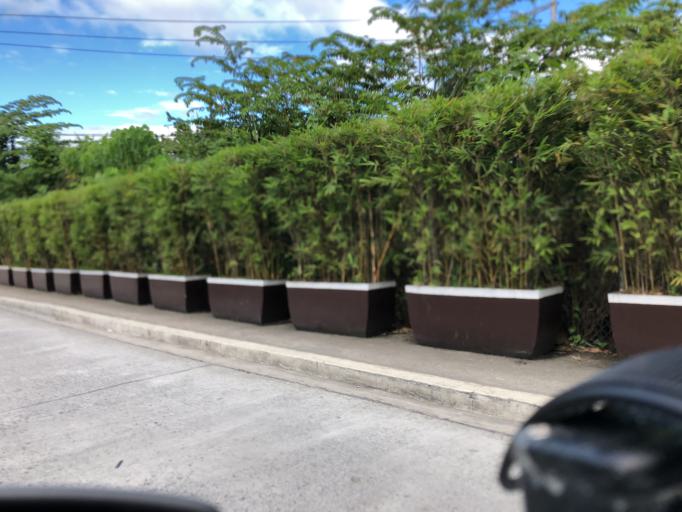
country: PH
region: Calabarzon
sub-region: Province of Rizal
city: San Mateo
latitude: 14.7381
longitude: 121.0601
